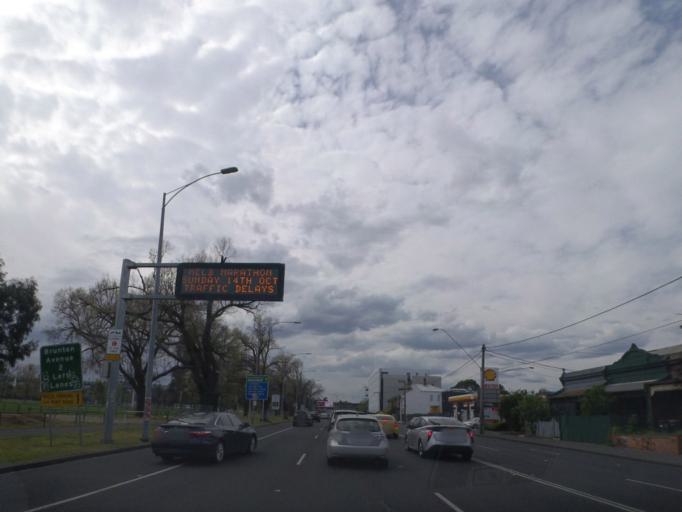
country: AU
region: Victoria
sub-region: Melbourne
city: East Melbourne
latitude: -37.8272
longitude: 144.9883
